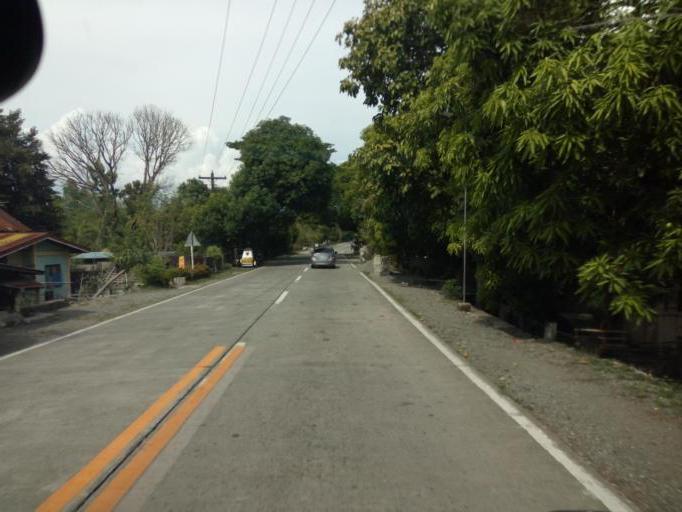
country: PH
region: Ilocos
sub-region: Province of Pangasinan
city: Umingan
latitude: 15.9138
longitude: 120.7658
